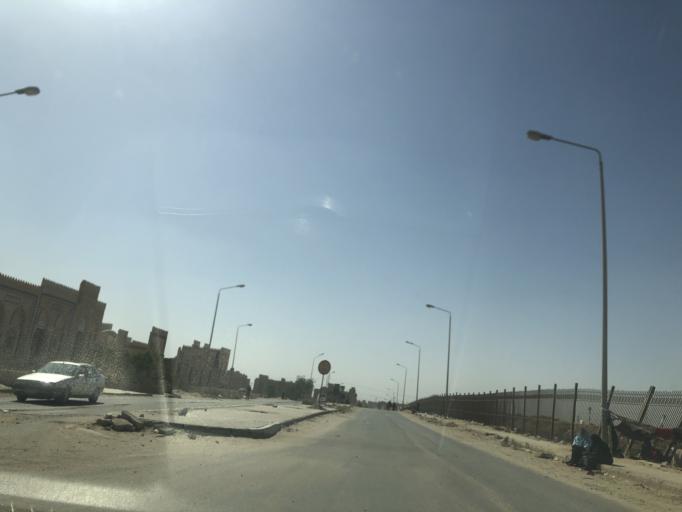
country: EG
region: Al Jizah
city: Madinat Sittah Uktubar
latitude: 29.9272
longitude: 30.9501
